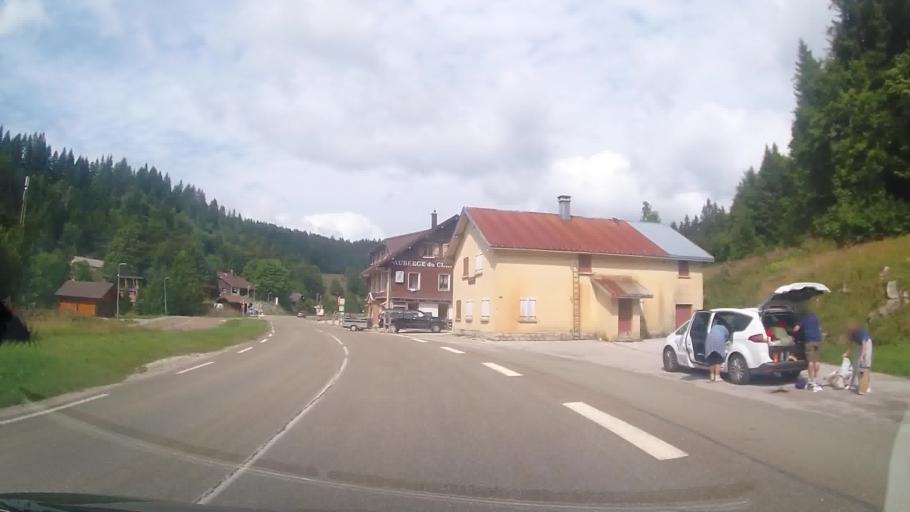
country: FR
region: Franche-Comte
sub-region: Departement du Jura
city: Les Rousses
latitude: 46.4289
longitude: 6.0717
